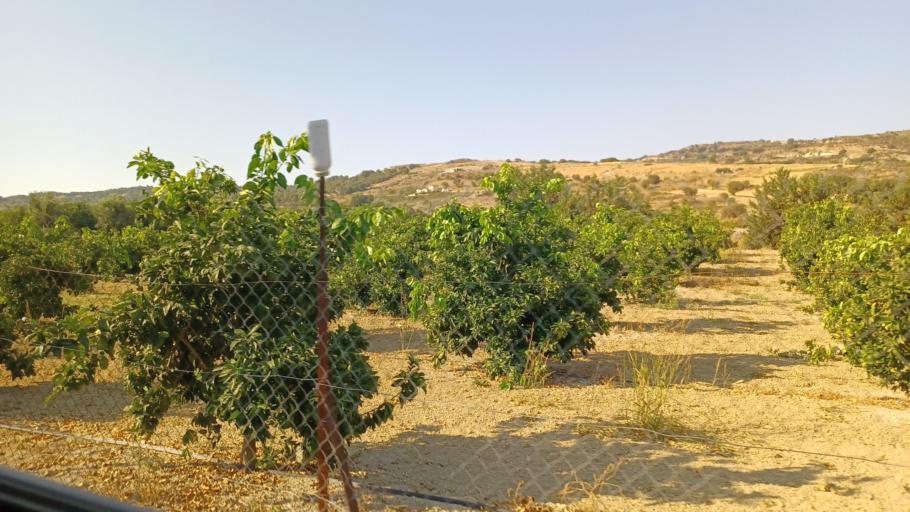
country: CY
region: Pafos
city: Tala
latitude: 34.9105
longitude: 32.4833
